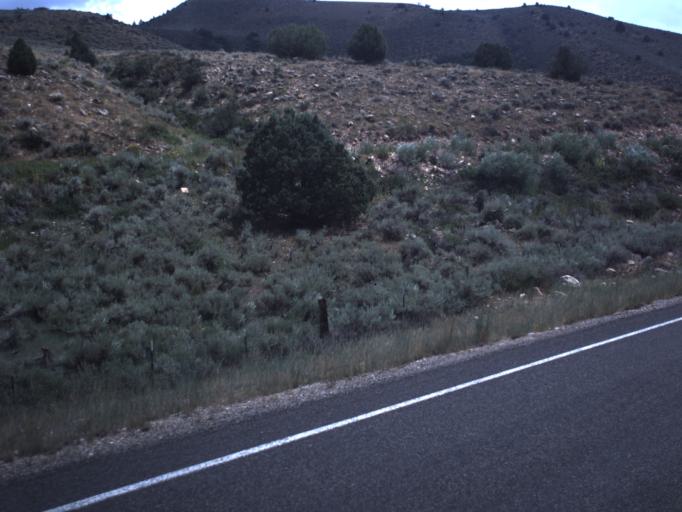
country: US
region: Utah
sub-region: Summit County
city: Francis
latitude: 40.4624
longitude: -110.8949
